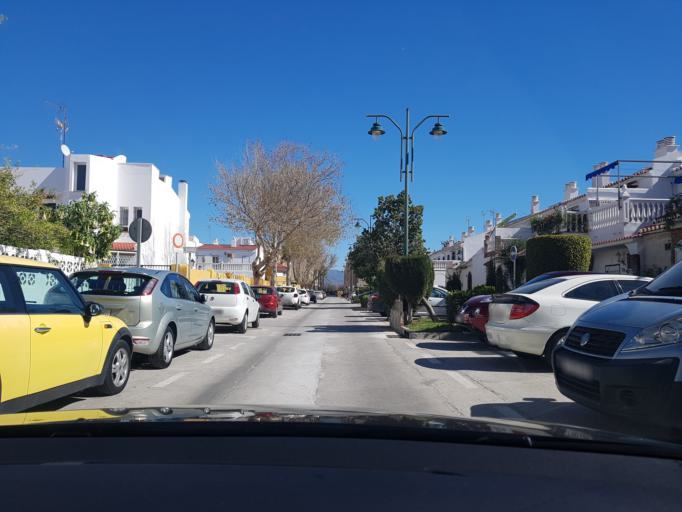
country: ES
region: Andalusia
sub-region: Provincia de Malaga
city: Torremolinos
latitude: 36.6636
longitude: -4.4593
